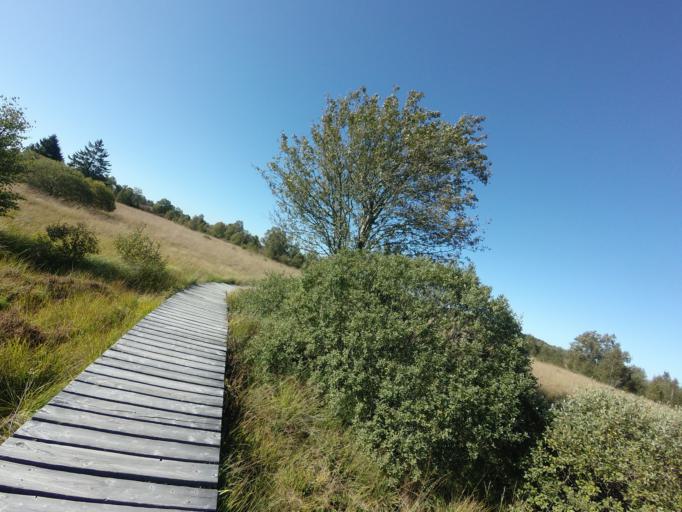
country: DE
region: North Rhine-Westphalia
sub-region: Regierungsbezirk Koln
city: Monschau
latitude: 50.5639
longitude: 6.1725
